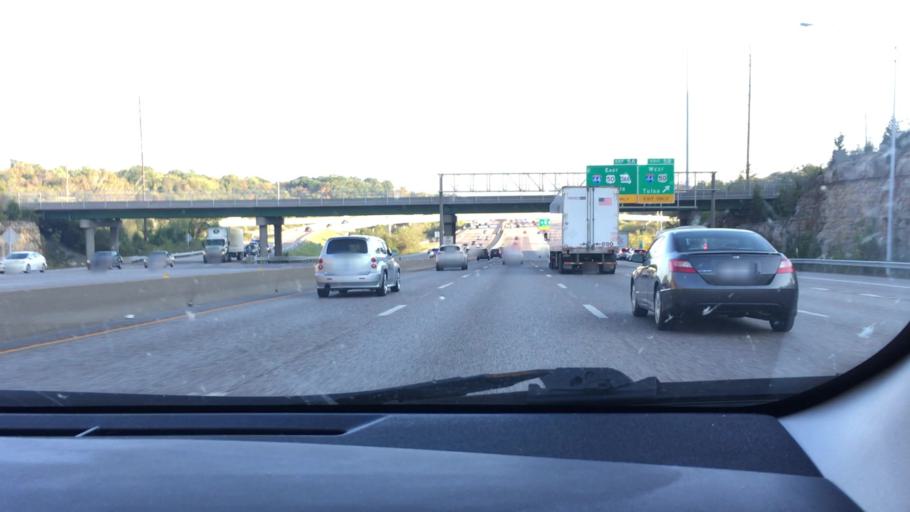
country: US
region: Missouri
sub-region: Saint Louis County
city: Sunset Hills
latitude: 38.5523
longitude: -90.4305
